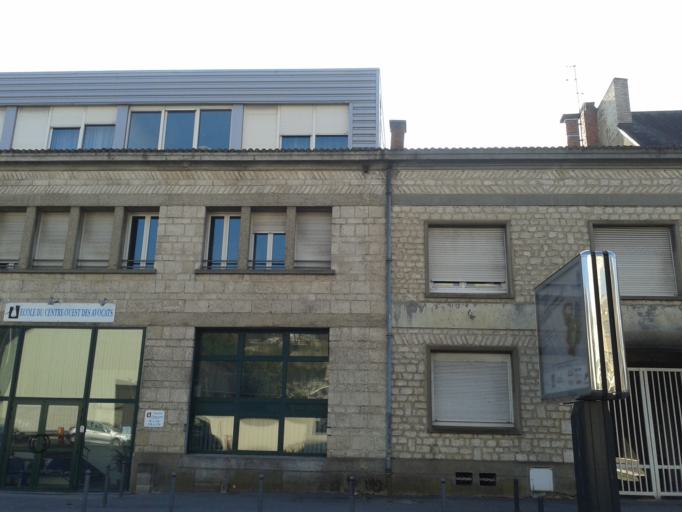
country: FR
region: Poitou-Charentes
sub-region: Departement de la Vienne
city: Poitiers
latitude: 46.5871
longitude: 0.3392
